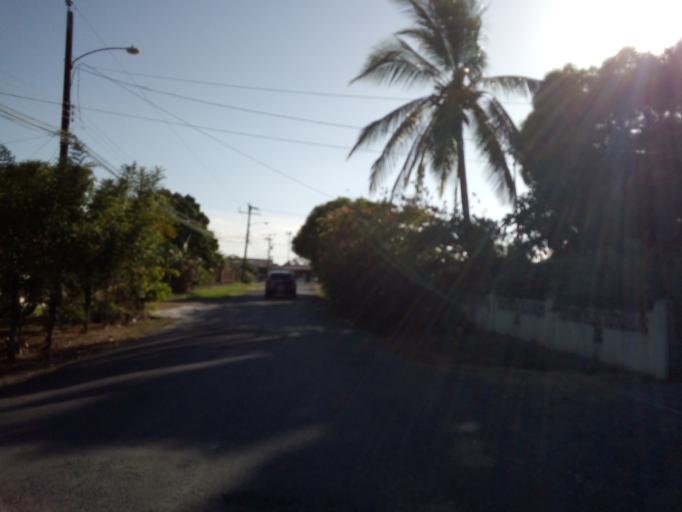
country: PA
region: Veraguas
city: Santiago de Veraguas
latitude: 8.1096
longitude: -80.9677
